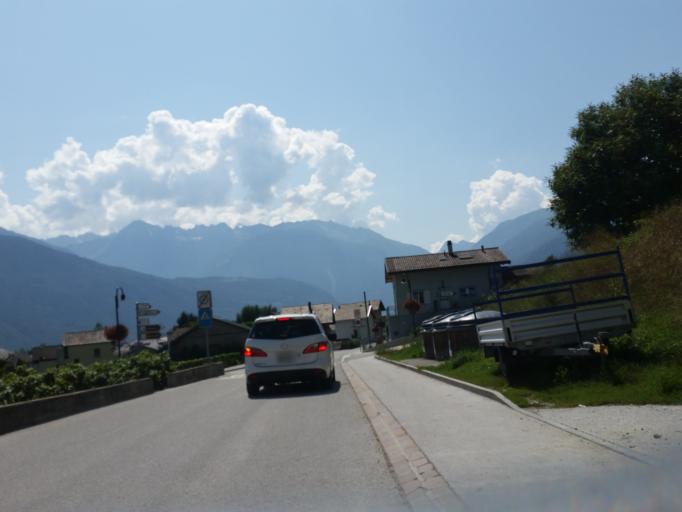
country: CH
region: Valais
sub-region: Martigny District
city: Fully
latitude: 46.1412
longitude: 7.1192
